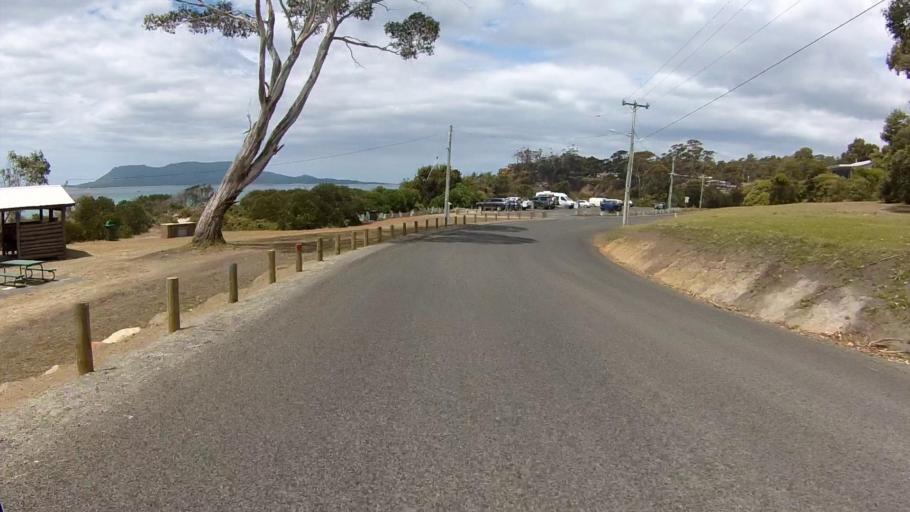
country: AU
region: Tasmania
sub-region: Sorell
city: Sorell
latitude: -42.5790
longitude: 147.9088
